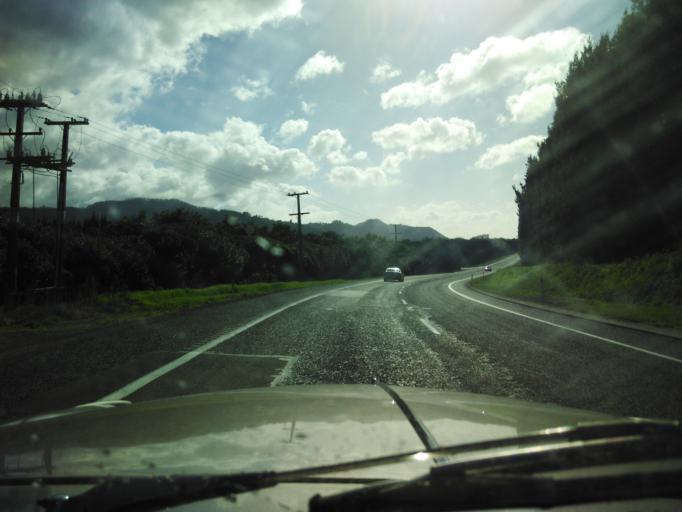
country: NZ
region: Bay of Plenty
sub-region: Western Bay of Plenty District
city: Katikati
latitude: -37.5136
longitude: 175.9192
